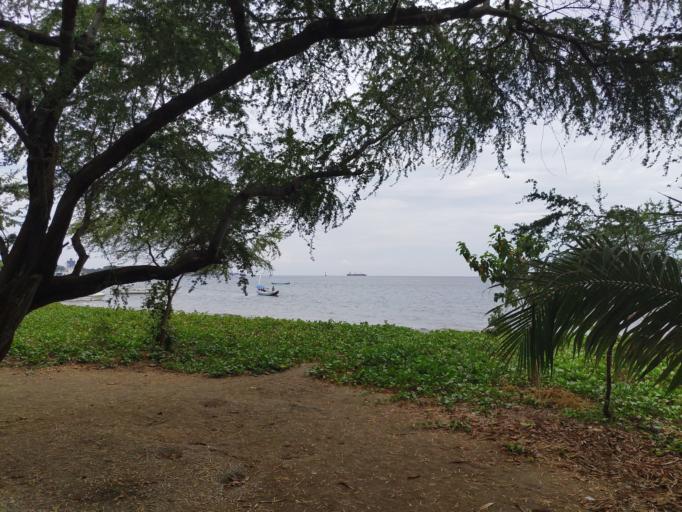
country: TL
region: Dili
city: Dili
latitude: -8.5508
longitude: 125.5833
